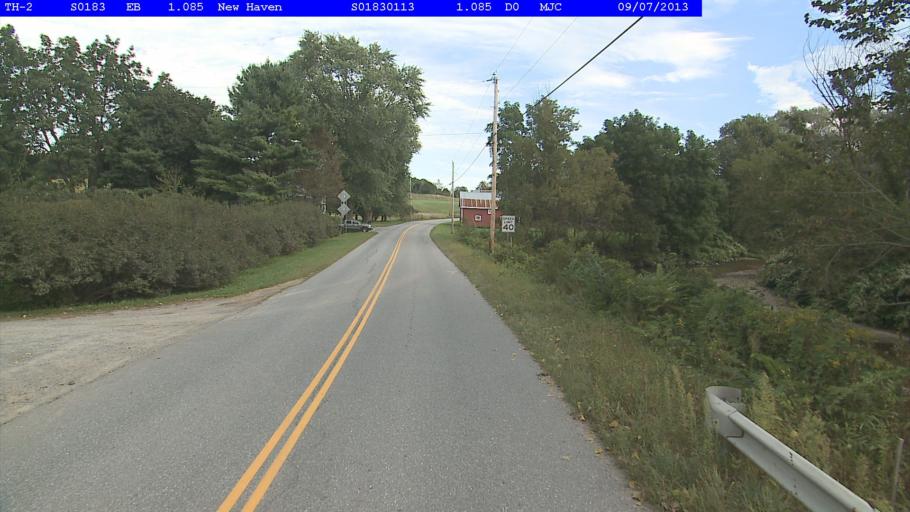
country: US
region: Vermont
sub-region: Addison County
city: Middlebury (village)
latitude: 44.0612
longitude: -73.1483
